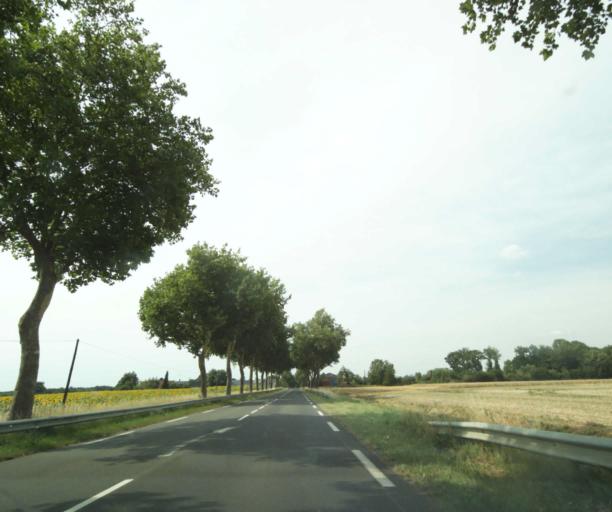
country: FR
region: Centre
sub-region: Departement d'Indre-et-Loire
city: Neuille-Pont-Pierre
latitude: 47.5708
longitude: 0.5465
